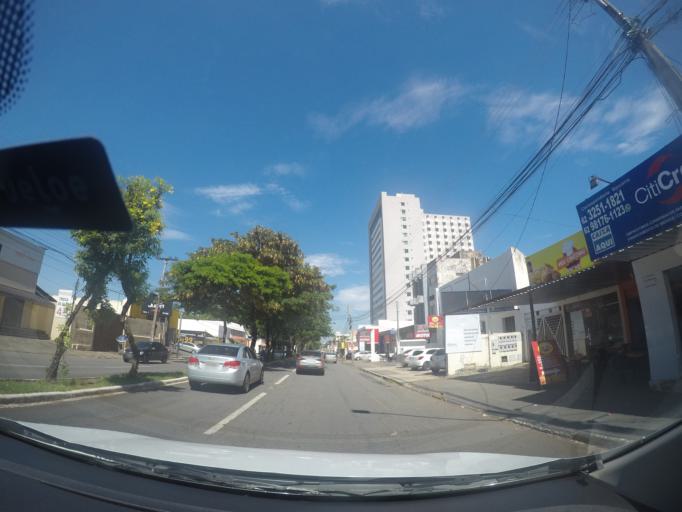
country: BR
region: Goias
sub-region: Goiania
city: Goiania
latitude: -16.7076
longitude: -49.2813
